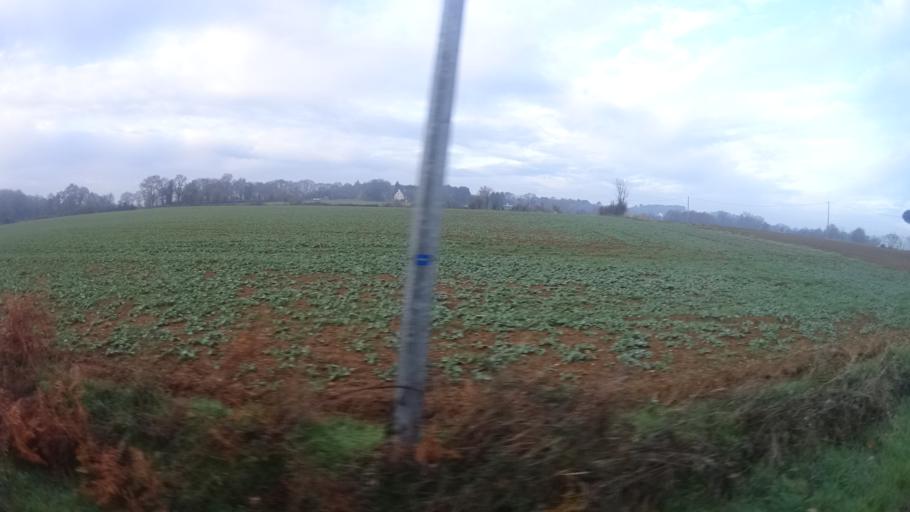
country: FR
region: Pays de la Loire
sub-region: Departement de la Loire-Atlantique
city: Avessac
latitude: 47.6479
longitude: -2.0243
